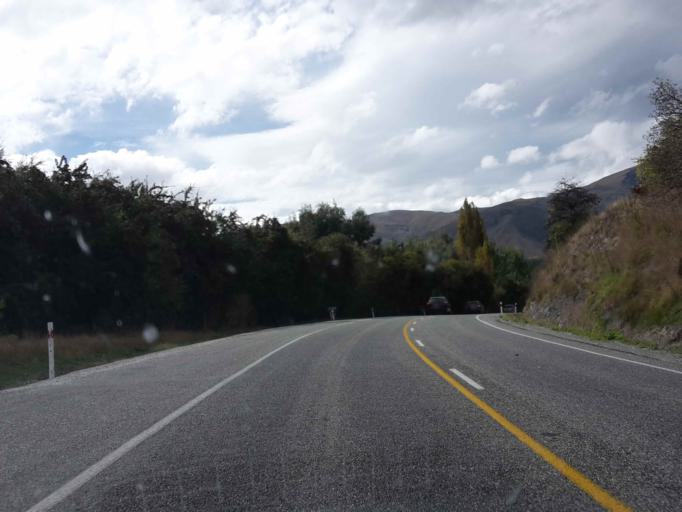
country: NZ
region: Otago
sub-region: Queenstown-Lakes District
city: Arrowtown
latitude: -44.9806
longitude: 168.8237
